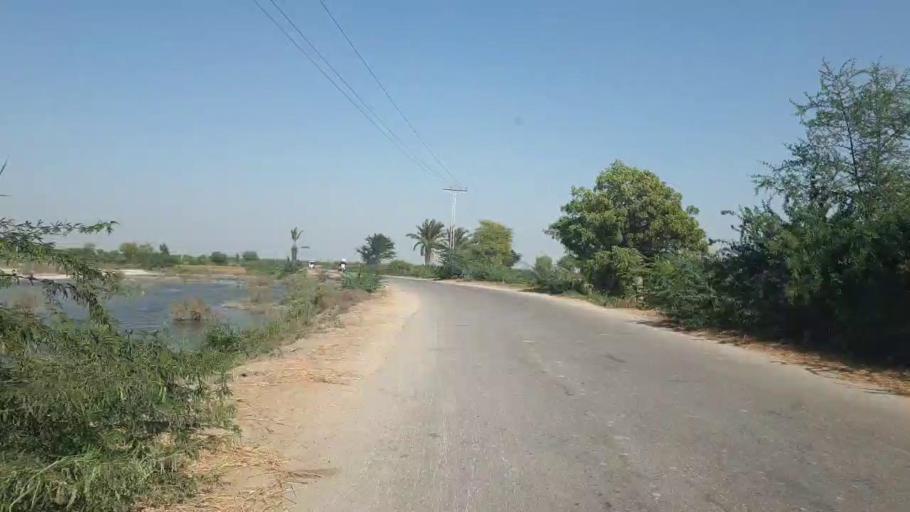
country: PK
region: Sindh
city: Talhar
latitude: 24.8970
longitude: 68.8262
